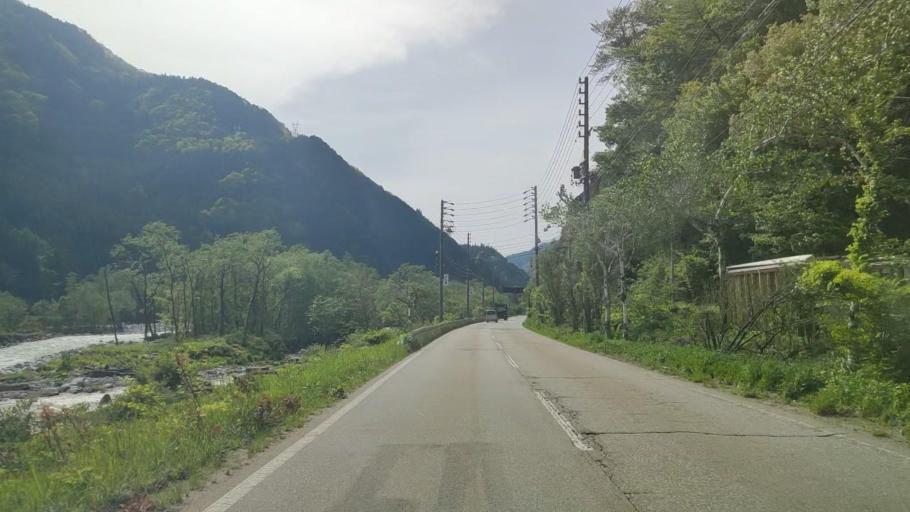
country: JP
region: Gifu
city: Takayama
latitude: 36.2499
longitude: 137.4844
